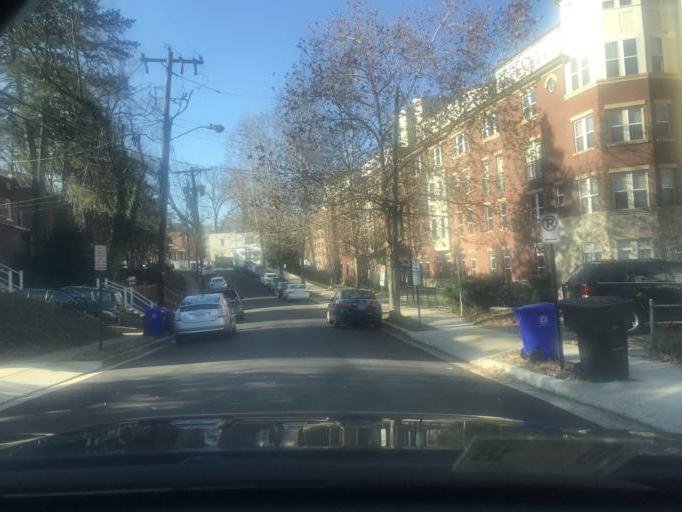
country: US
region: Virginia
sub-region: Arlington County
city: Arlington
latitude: 38.8978
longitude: -77.0770
